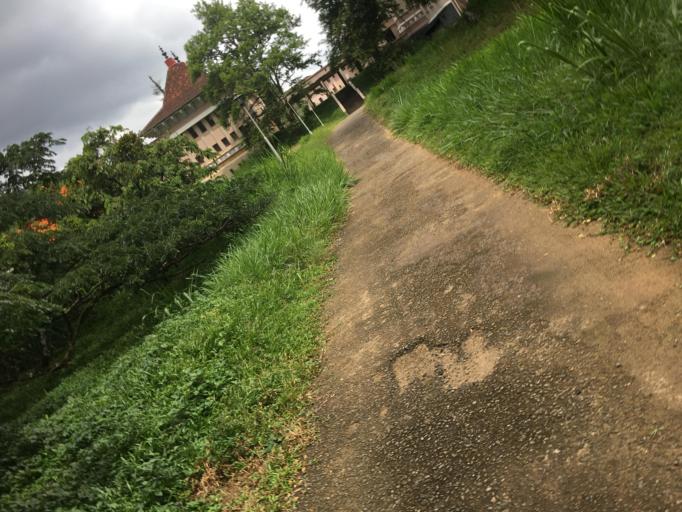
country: LK
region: Central
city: Kandy
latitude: 7.2556
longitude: 80.5968
